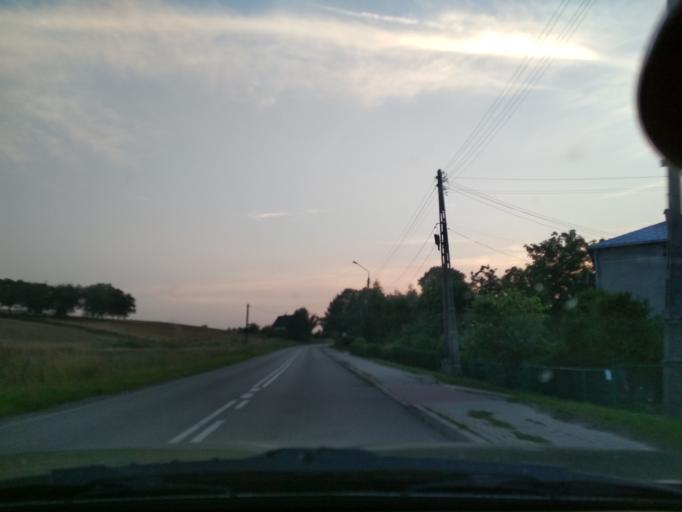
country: PL
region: Silesian Voivodeship
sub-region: Powiat zawiercianski
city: Pilica
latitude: 50.4666
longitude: 19.7096
